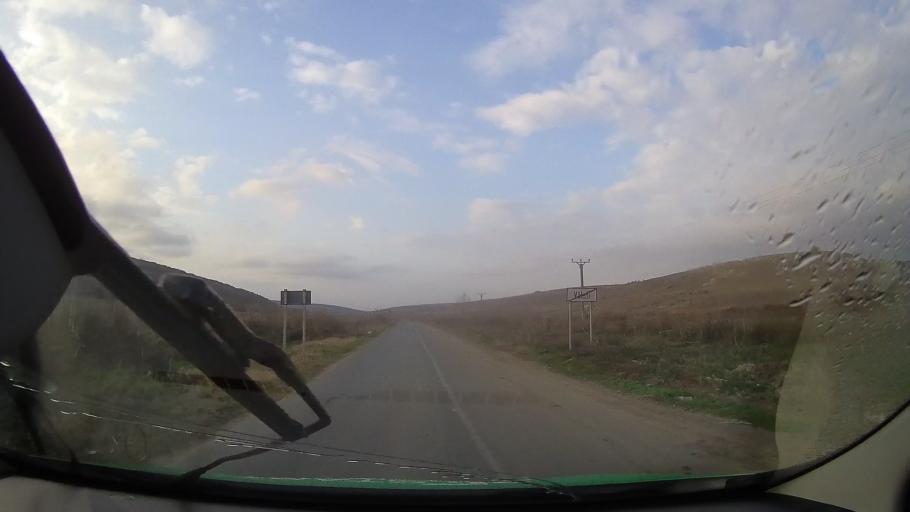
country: RO
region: Constanta
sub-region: Comuna Dobromir
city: Dobromir
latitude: 44.0220
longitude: 27.8705
